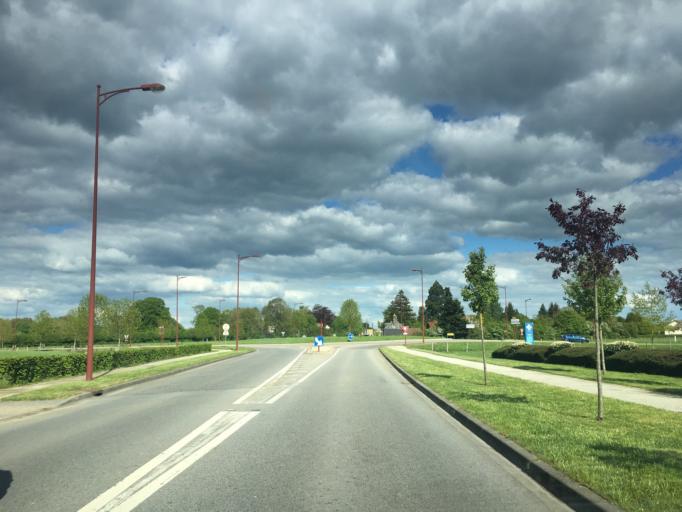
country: FR
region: Lower Normandy
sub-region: Departement de l'Orne
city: Saint-Sulpice-sur-Risle
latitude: 48.7618
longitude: 0.6471
